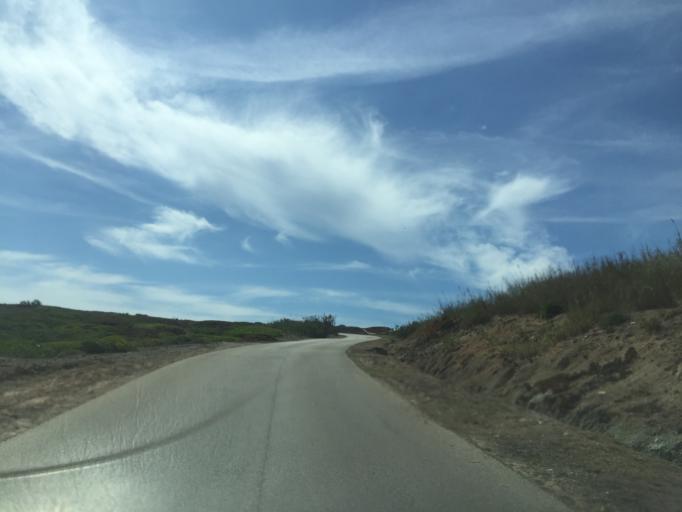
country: PT
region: Lisbon
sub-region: Lourinha
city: Lourinha
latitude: 39.1824
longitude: -9.3532
